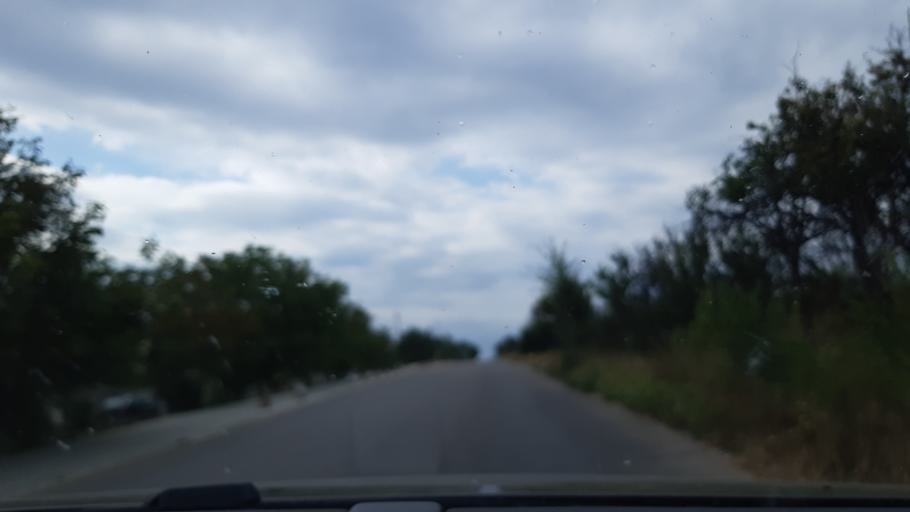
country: MD
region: Chisinau
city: Vatra
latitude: 47.0434
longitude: 28.7479
